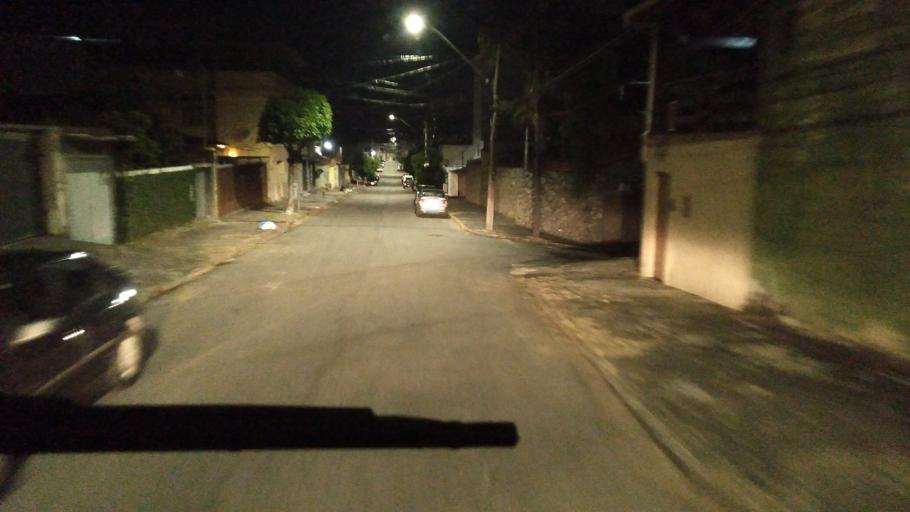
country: BR
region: Minas Gerais
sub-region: Belo Horizonte
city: Belo Horizonte
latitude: -19.8737
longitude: -43.9440
